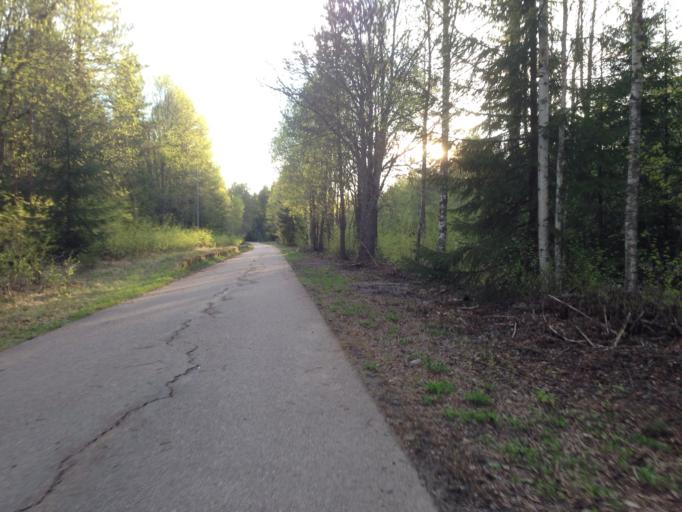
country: SE
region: Dalarna
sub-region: Ludvika Kommun
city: Ludvika
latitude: 60.1413
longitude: 15.1031
